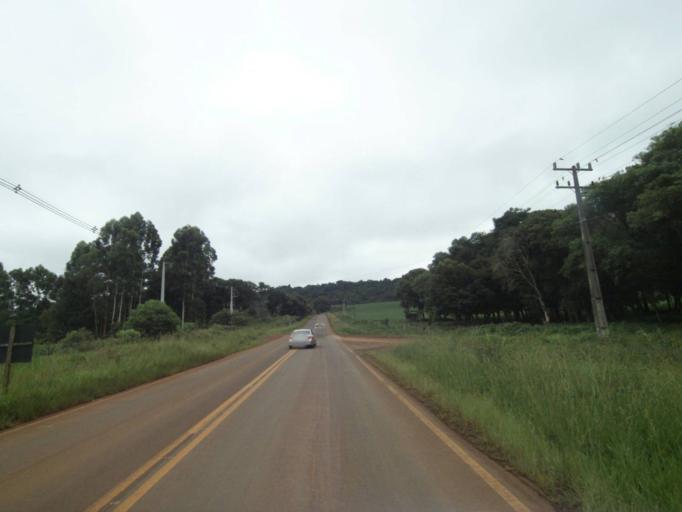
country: BR
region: Parana
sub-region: Pitanga
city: Pitanga
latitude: -24.9245
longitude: -51.8722
